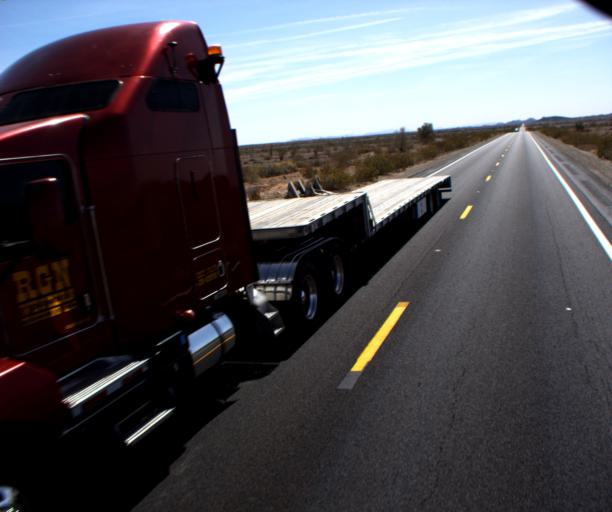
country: US
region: Arizona
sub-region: Yuma County
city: Wellton
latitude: 33.1466
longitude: -114.2841
